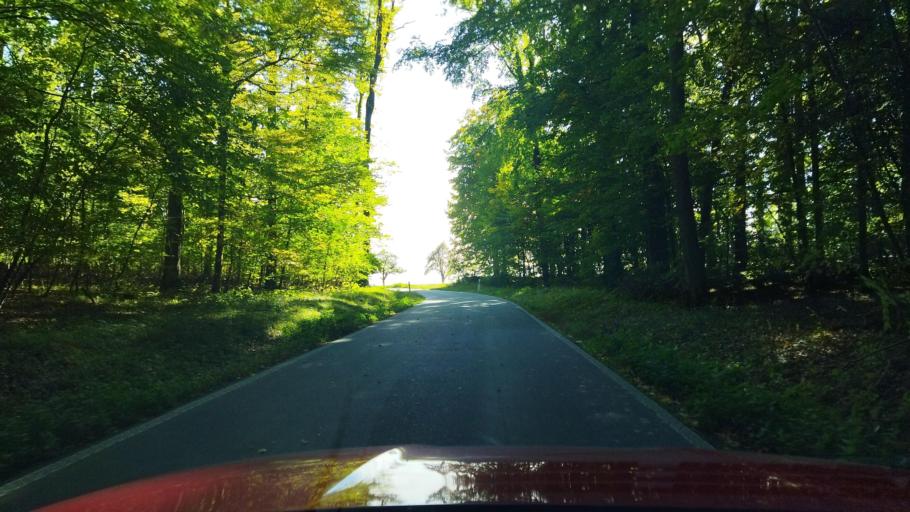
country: DE
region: Baden-Wuerttemberg
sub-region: Karlsruhe Region
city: Sulzfeld
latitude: 49.0816
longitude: 8.8860
